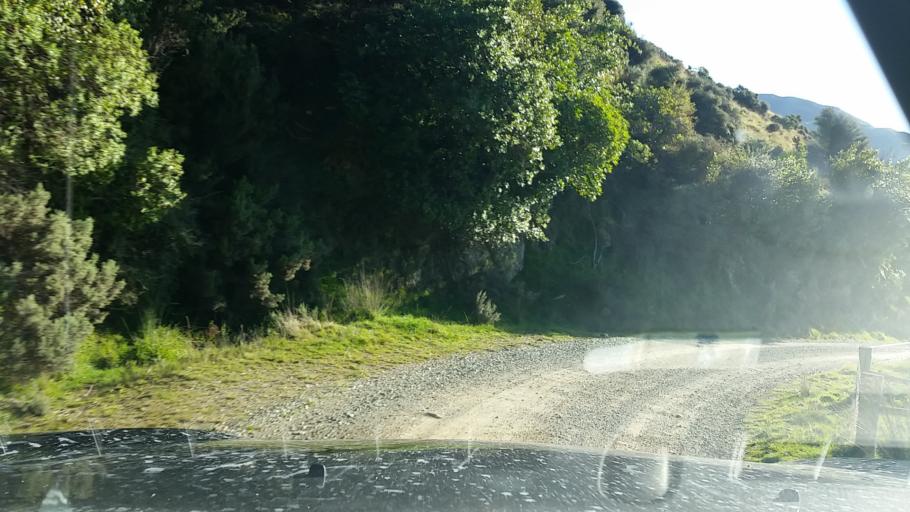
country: NZ
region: Marlborough
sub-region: Marlborough District
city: Picton
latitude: -41.0239
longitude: 174.1461
